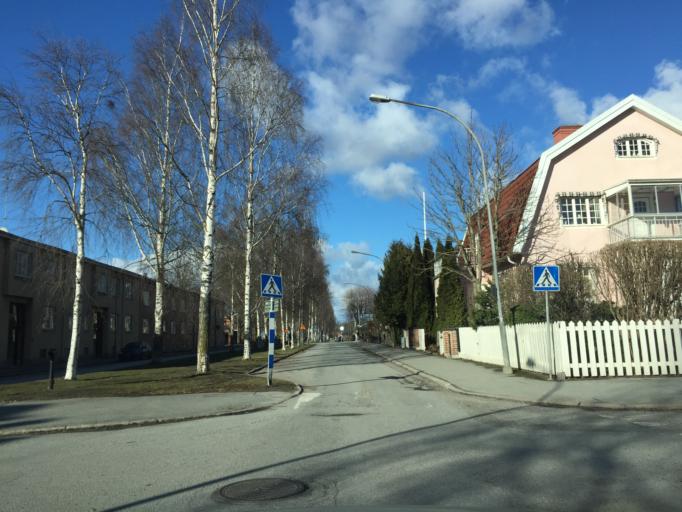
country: SE
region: OErebro
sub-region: Orebro Kommun
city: Orebro
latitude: 59.2695
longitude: 15.2357
